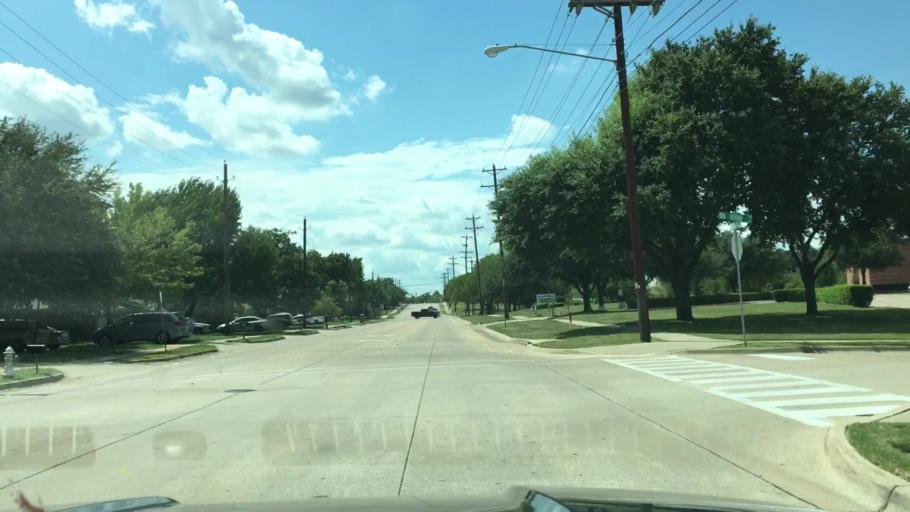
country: US
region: Texas
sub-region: Tarrant County
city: Keller
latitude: 32.9417
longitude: -97.2486
